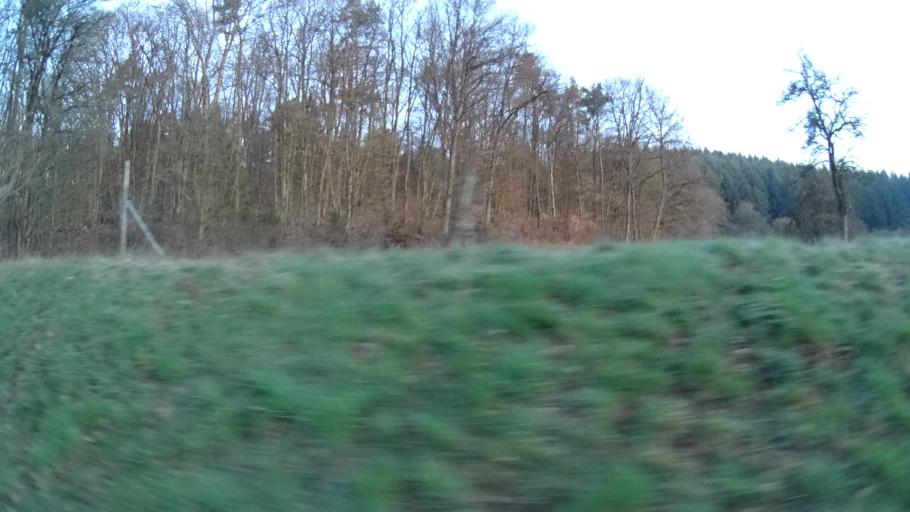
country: DE
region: Rheinland-Pfalz
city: Langweiler
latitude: 49.6667
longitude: 7.5073
